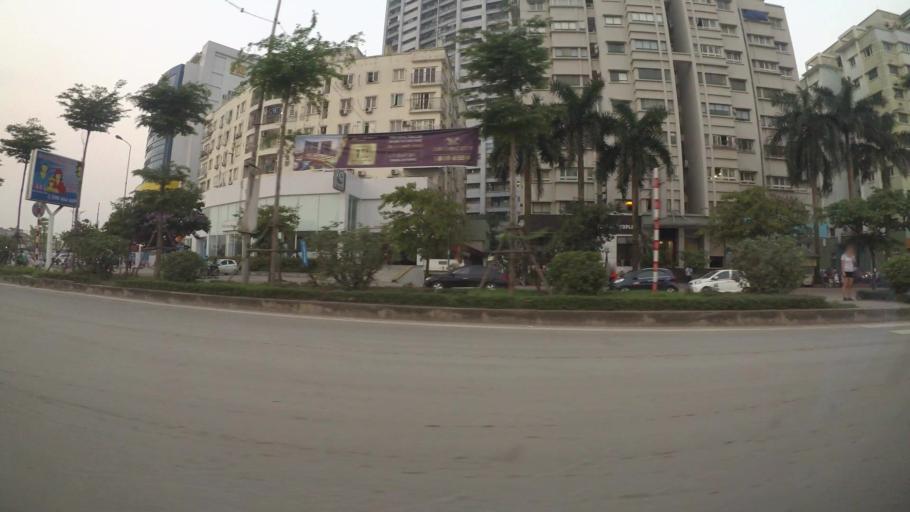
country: VN
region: Ha Noi
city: Tay Ho
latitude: 21.0681
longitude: 105.7862
